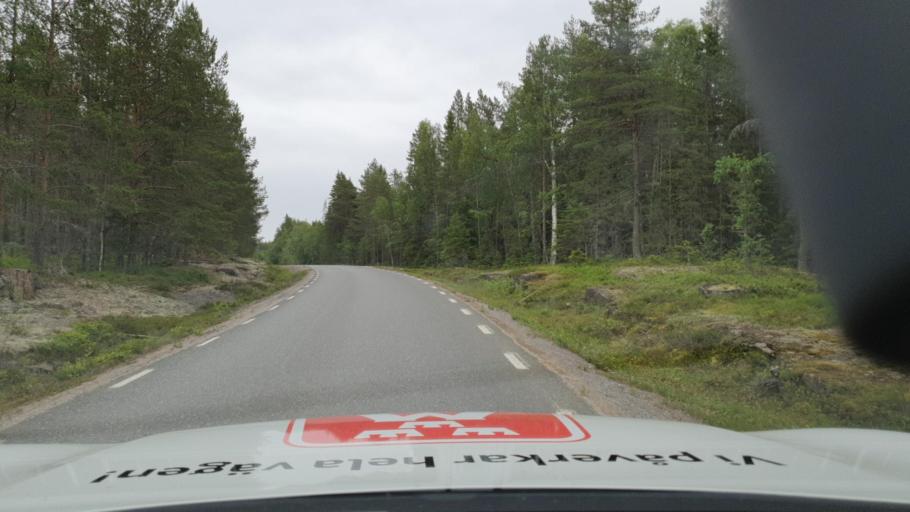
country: SE
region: Vaesterbotten
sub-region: Nordmalings Kommun
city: Nordmaling
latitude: 63.4334
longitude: 19.4752
